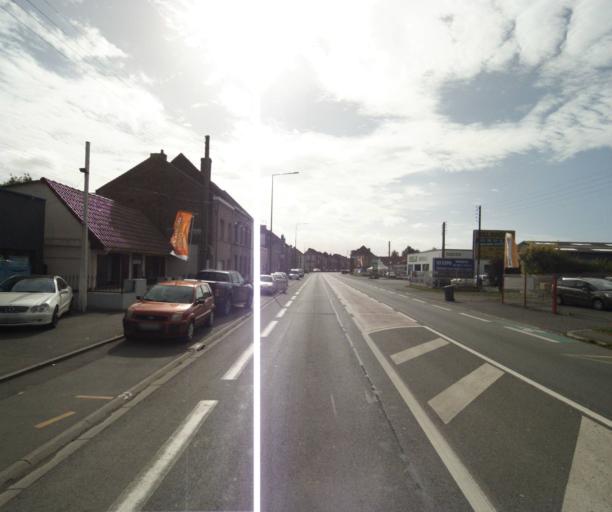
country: FR
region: Nord-Pas-de-Calais
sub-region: Departement du Nord
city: La Bassee
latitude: 50.5360
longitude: 2.8150
